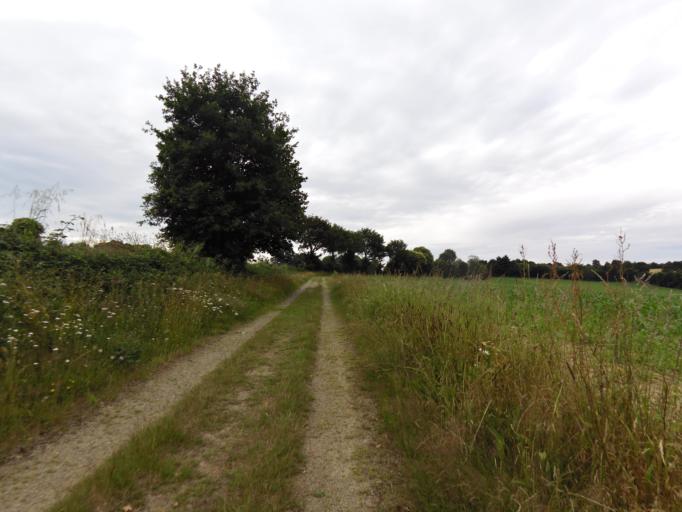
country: FR
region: Brittany
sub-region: Departement d'Ille-et-Vilaine
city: Chanteloup
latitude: 47.9319
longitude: -1.5971
